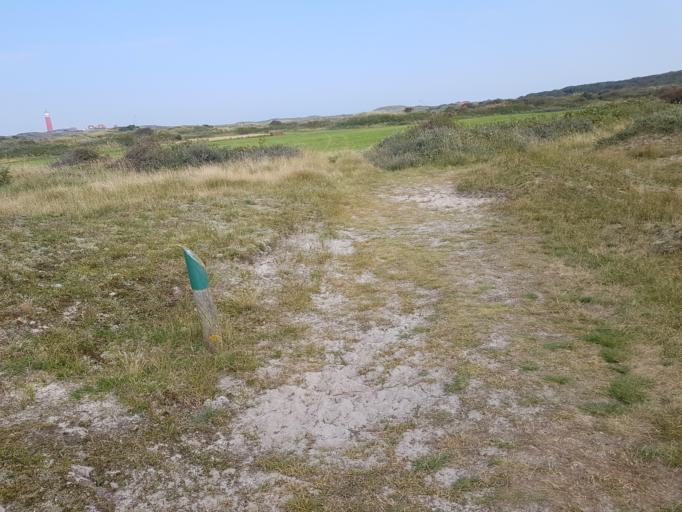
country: NL
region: North Holland
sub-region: Gemeente Texel
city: Den Burg
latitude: 53.1744
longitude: 4.8479
